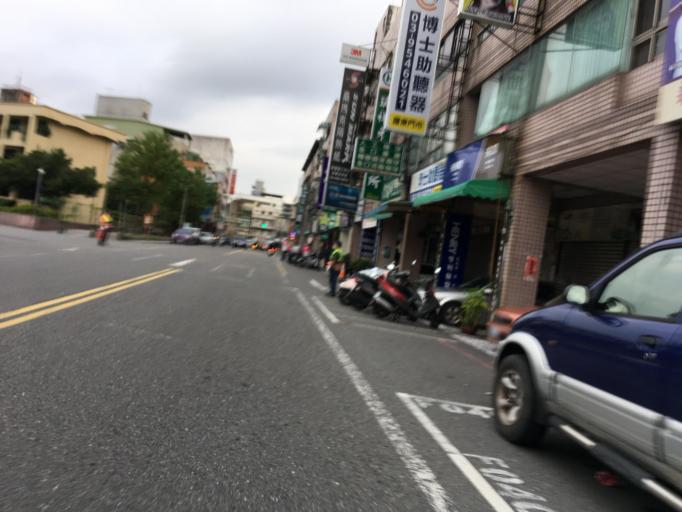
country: TW
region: Taiwan
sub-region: Yilan
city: Yilan
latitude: 24.6717
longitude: 121.7678
